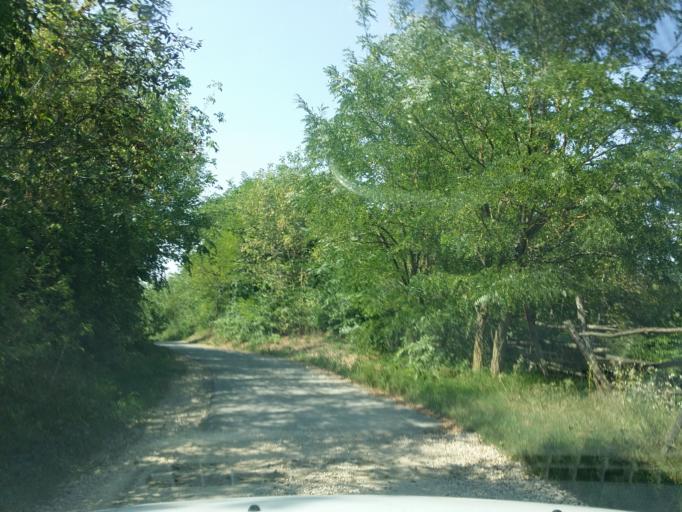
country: HU
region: Tolna
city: Gyonk
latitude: 46.5854
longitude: 18.4023
